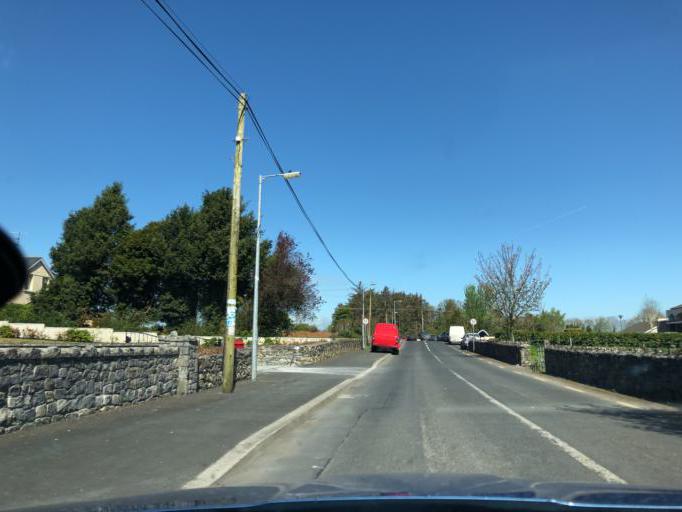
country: IE
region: Connaught
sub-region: County Galway
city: Portumna
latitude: 53.1442
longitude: -8.3686
